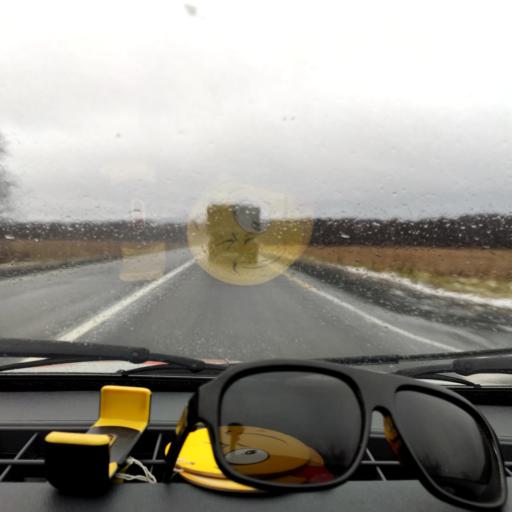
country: RU
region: Bashkortostan
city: Urman
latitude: 54.8175
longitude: 56.8573
